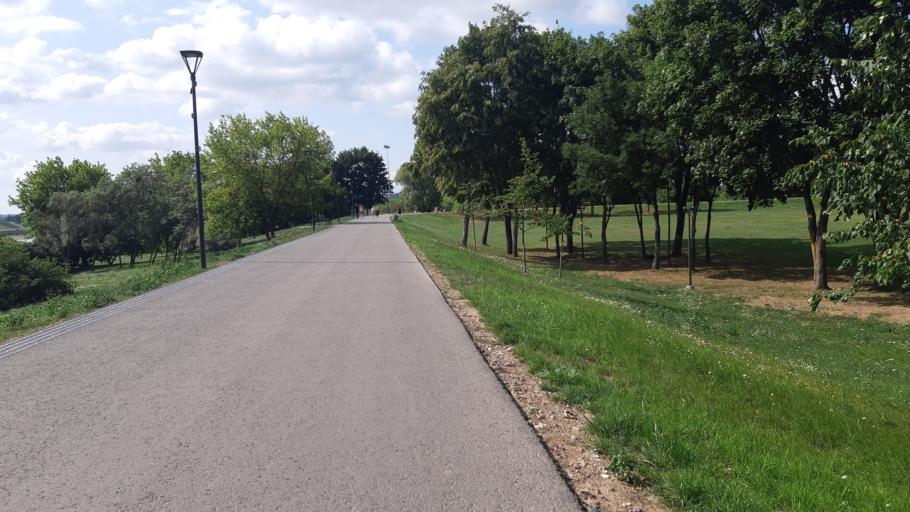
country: LT
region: Kauno apskritis
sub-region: Kaunas
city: Kaunas
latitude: 54.8973
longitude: 23.8791
